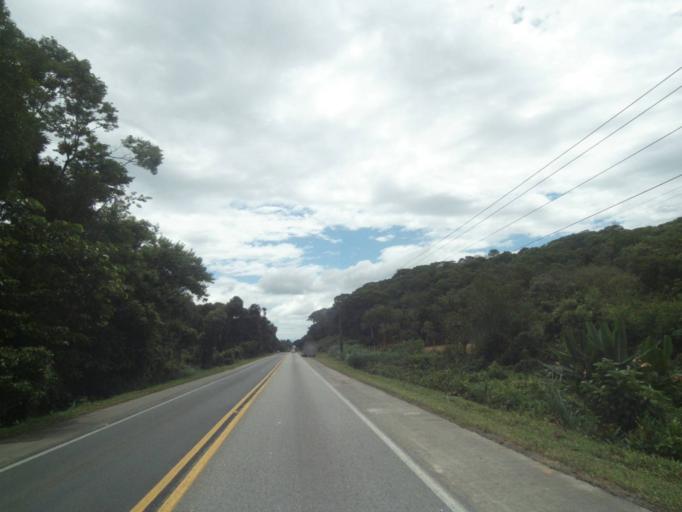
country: BR
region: Parana
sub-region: Antonina
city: Antonina
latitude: -25.4461
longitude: -48.7693
